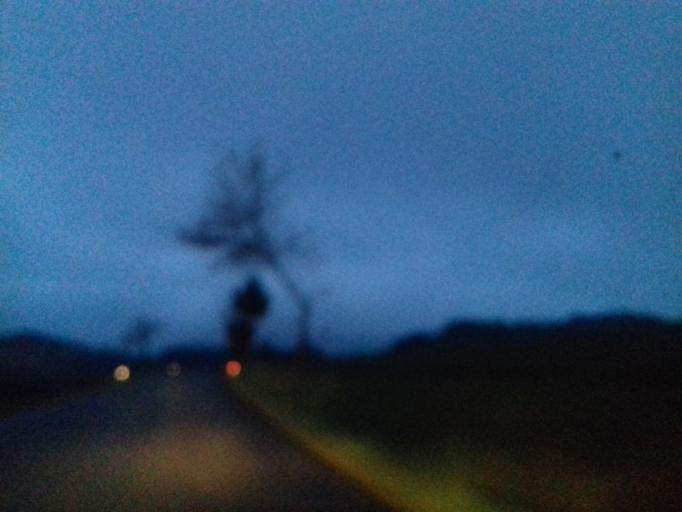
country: CZ
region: South Moravian
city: Olesnice
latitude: 49.5852
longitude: 16.3804
